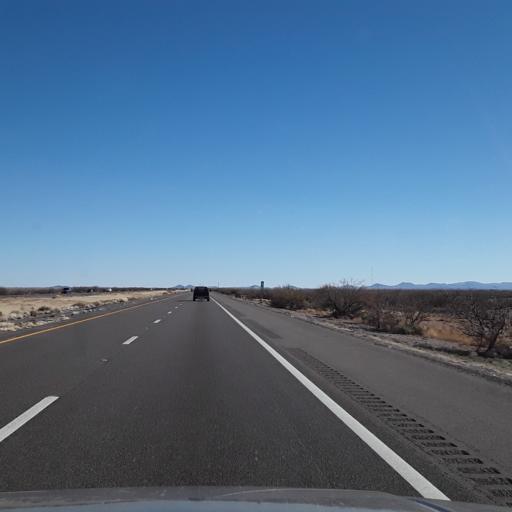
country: US
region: New Mexico
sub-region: Luna County
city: Deming
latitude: 32.2595
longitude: -107.4986
